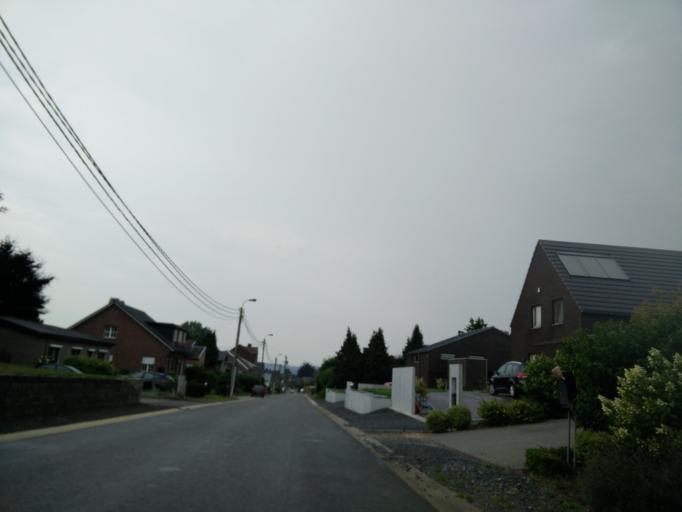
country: BE
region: Wallonia
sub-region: Province de Liege
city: Dalhem
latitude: 50.7302
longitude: 5.7633
